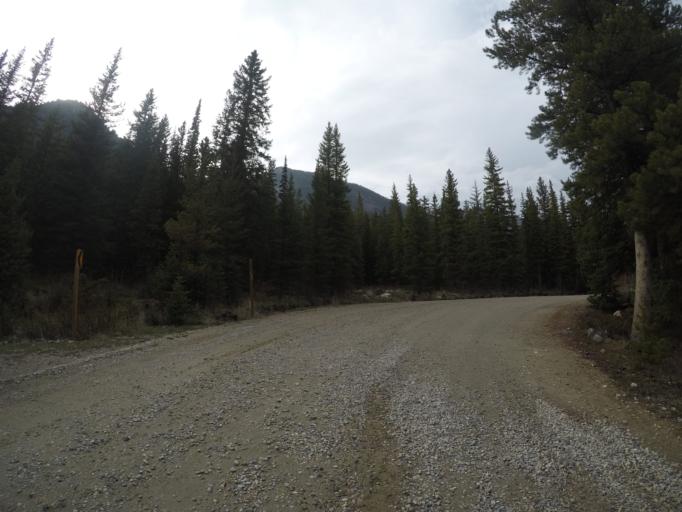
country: US
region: Montana
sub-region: Carbon County
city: Red Lodge
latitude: 45.0419
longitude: -109.4275
